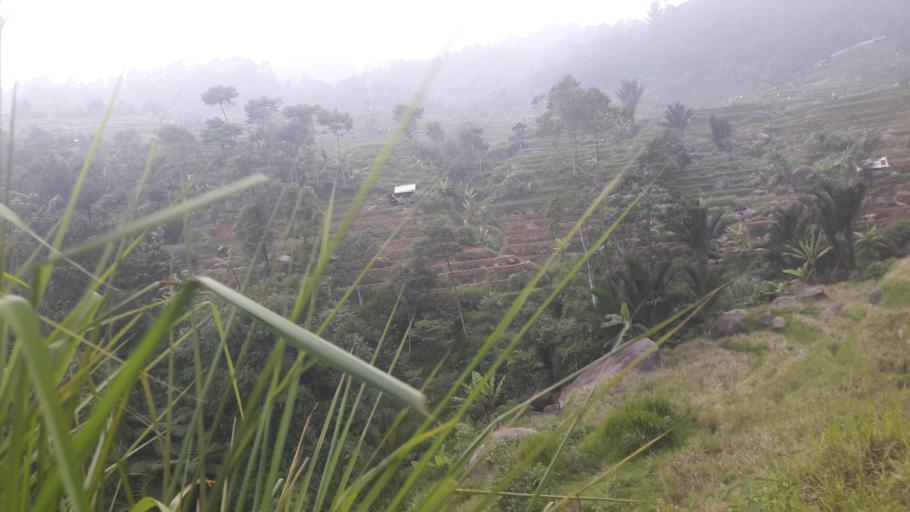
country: ID
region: West Java
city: Cipeundeuy
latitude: -6.6803
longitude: 106.5247
